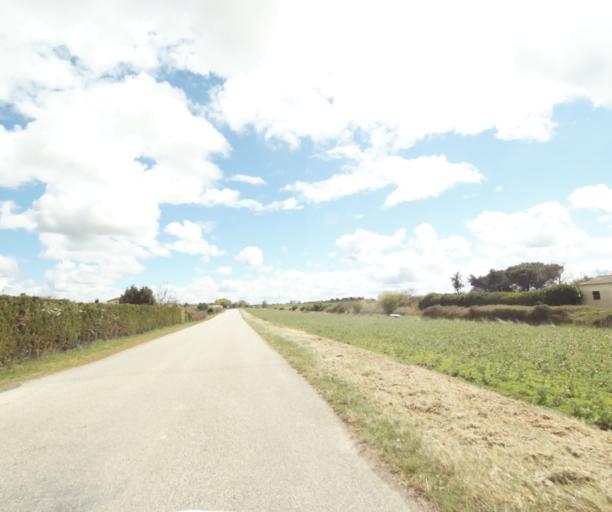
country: FR
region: Midi-Pyrenees
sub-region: Departement de l'Ariege
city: Saverdun
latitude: 43.2392
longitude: 1.5888
